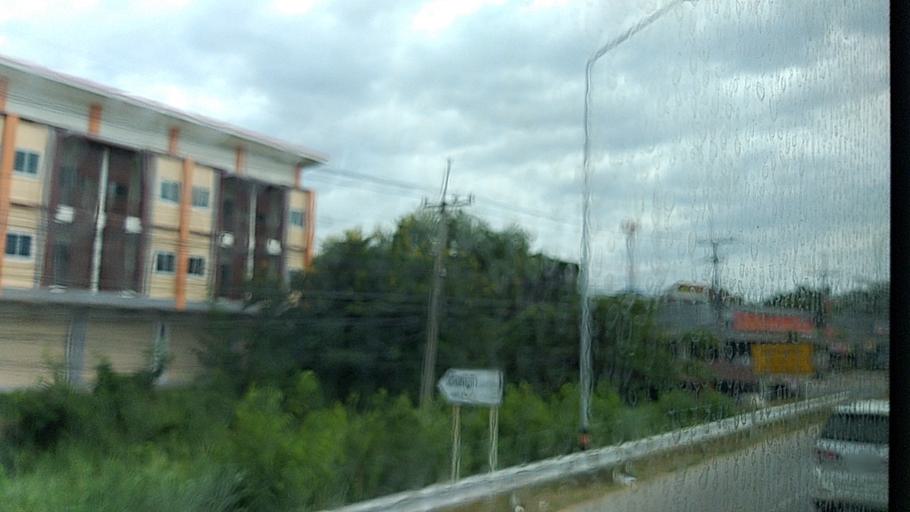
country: TH
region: Maha Sarakham
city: Maha Sarakham
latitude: 16.2075
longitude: 103.2856
